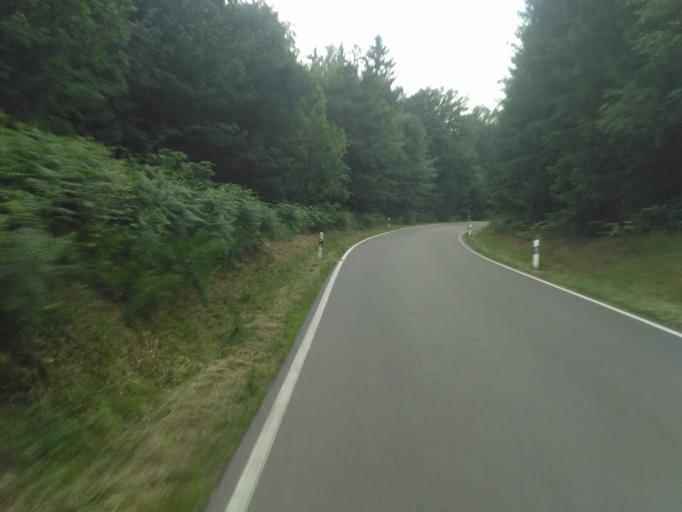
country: DE
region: Saxony
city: Kurort Gohrisch
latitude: 50.8962
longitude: 14.1093
